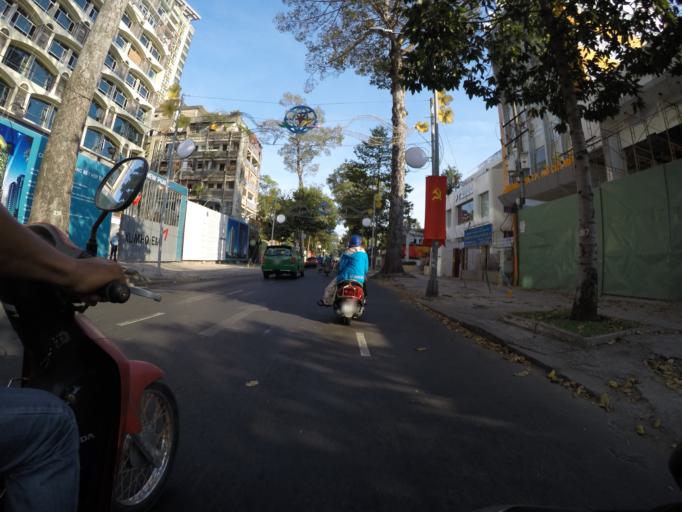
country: VN
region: Ho Chi Minh City
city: Quan Mot
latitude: 10.7822
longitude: 106.6921
